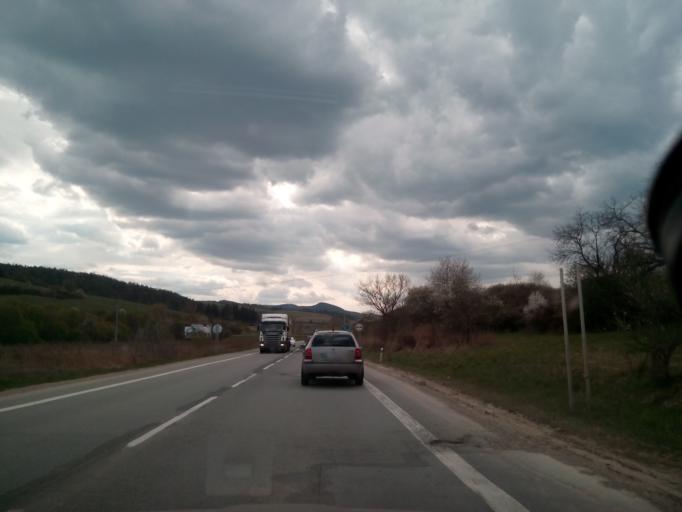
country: SK
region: Presovsky
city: Lipany
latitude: 49.0215
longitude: 20.9904
